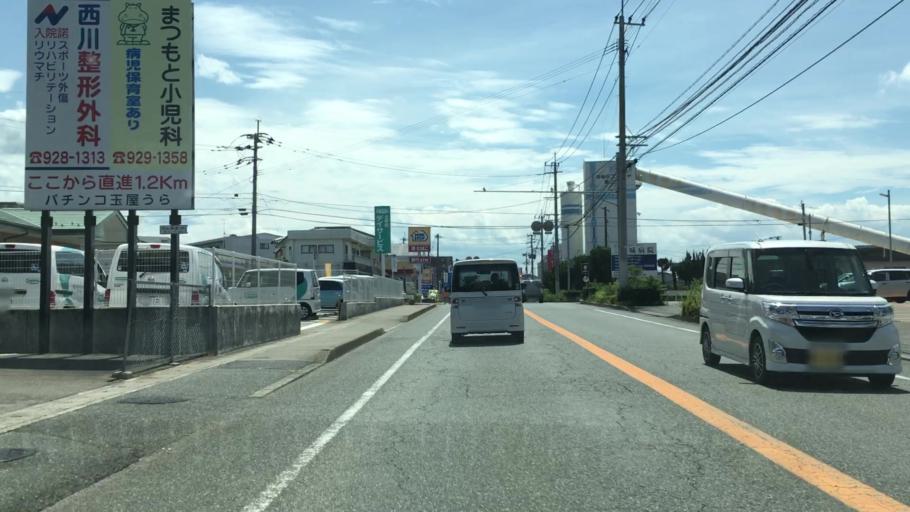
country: JP
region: Fukuoka
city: Dazaifu
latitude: 33.5168
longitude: 130.5036
